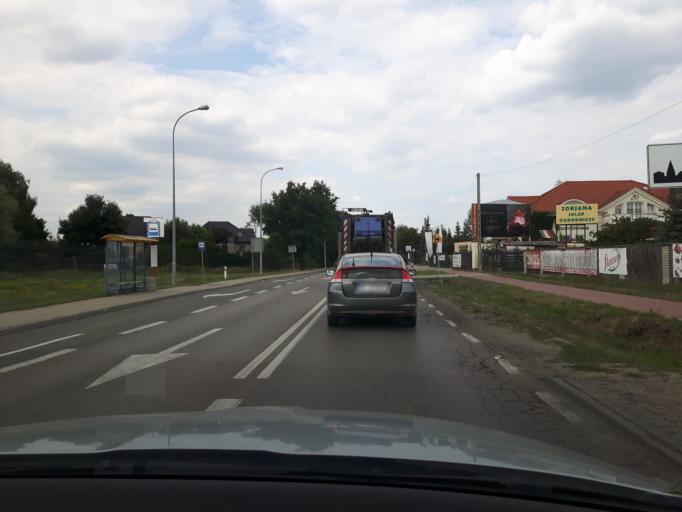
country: PL
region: Masovian Voivodeship
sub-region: Powiat legionowski
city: Stanislawow Pierwszy
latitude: 52.3648
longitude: 21.0283
